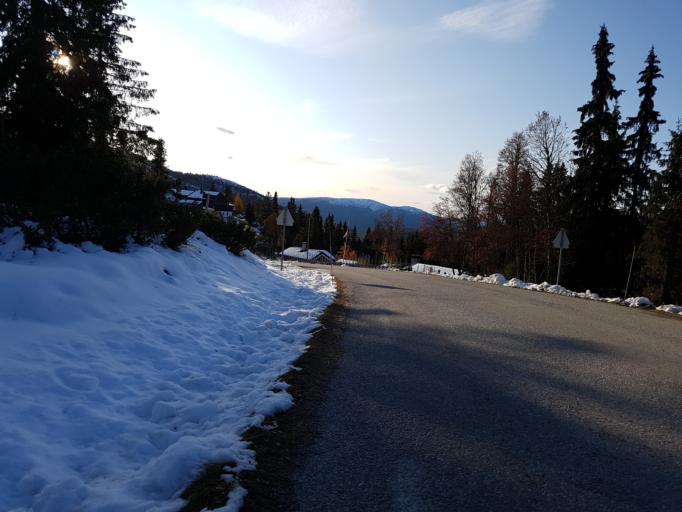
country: NO
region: Oppland
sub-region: Sel
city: Otta
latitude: 61.8094
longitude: 9.6775
